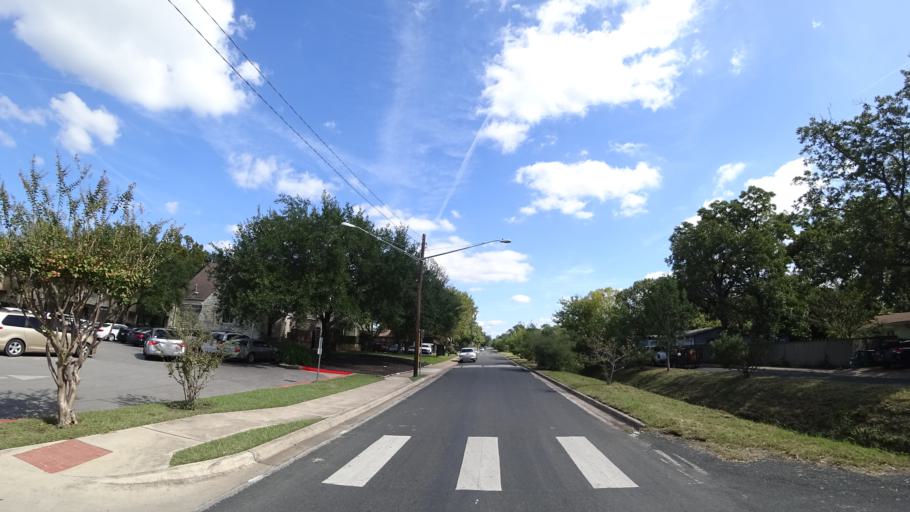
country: US
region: Texas
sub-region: Travis County
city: Austin
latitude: 30.3517
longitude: -97.7321
